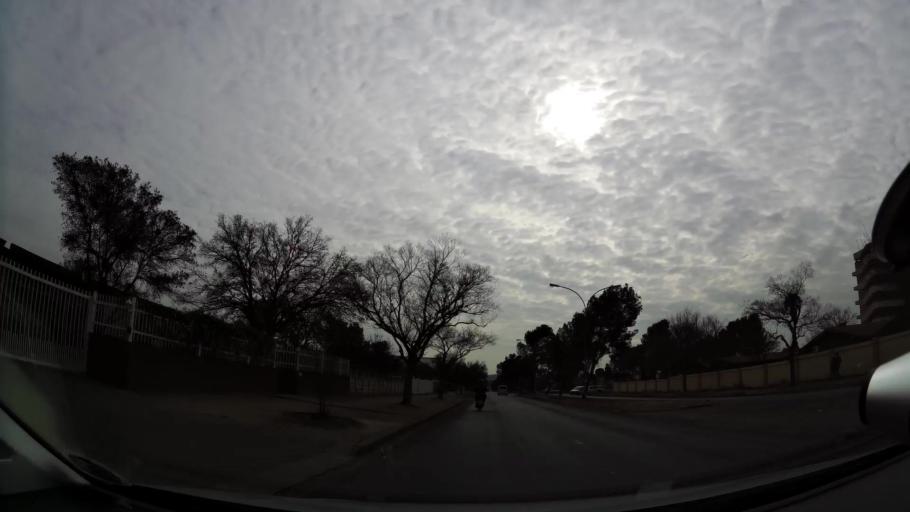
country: ZA
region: Orange Free State
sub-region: Mangaung Metropolitan Municipality
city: Bloemfontein
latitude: -29.1265
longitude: 26.2023
